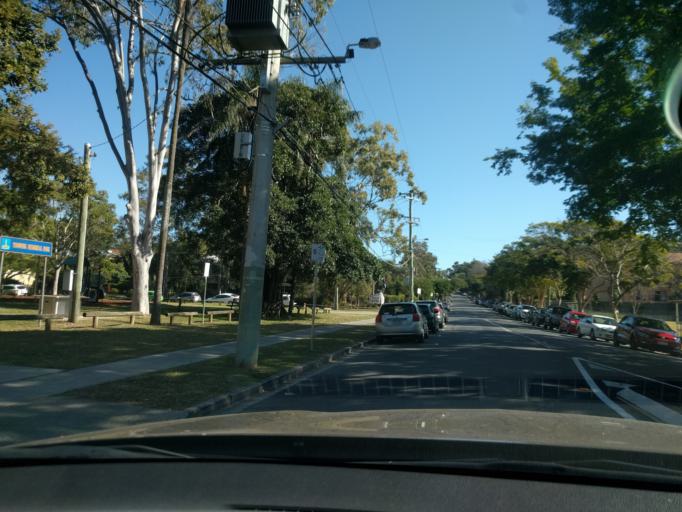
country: AU
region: Queensland
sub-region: Brisbane
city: Toowong
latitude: -27.4781
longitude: 152.9959
